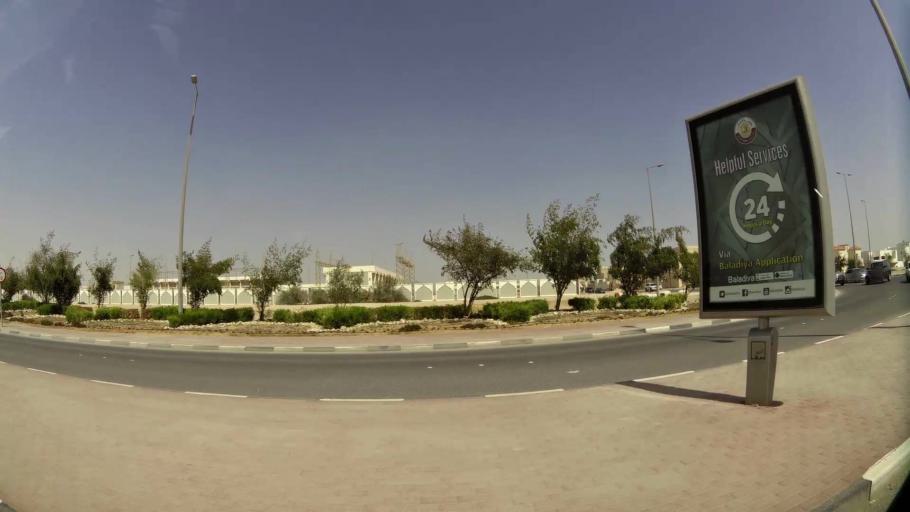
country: QA
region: Baladiyat Umm Salal
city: Umm Salal Muhammad
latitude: 25.3755
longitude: 51.4314
